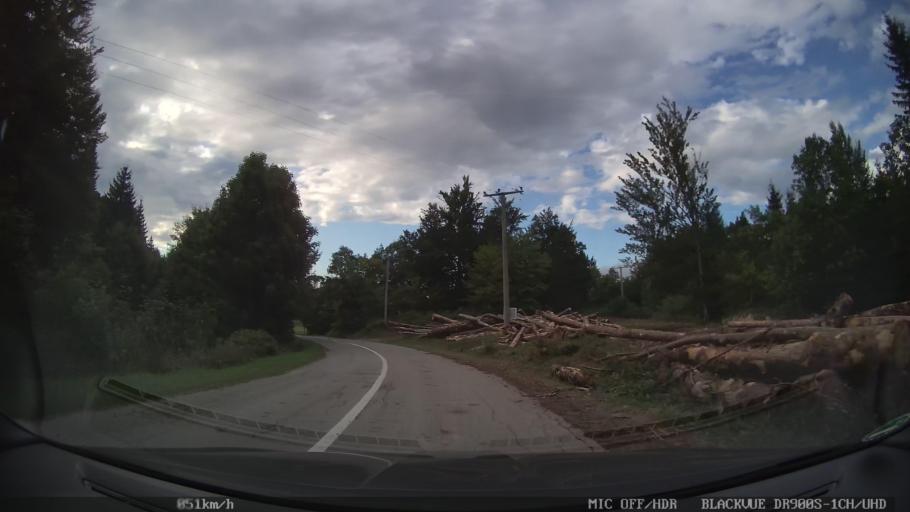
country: HR
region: Licko-Senjska
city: Jezerce
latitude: 44.9624
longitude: 15.5268
